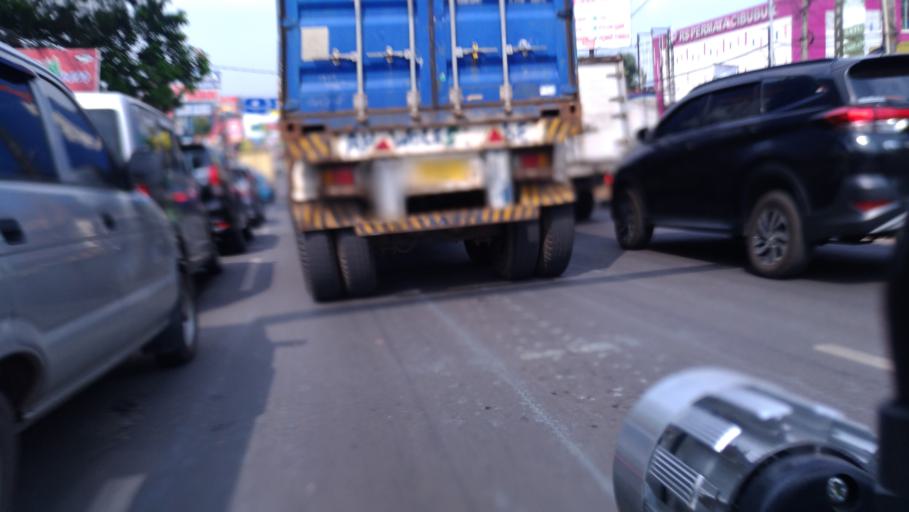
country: ID
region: West Java
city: Cileungsir
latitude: -6.3754
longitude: 106.9114
